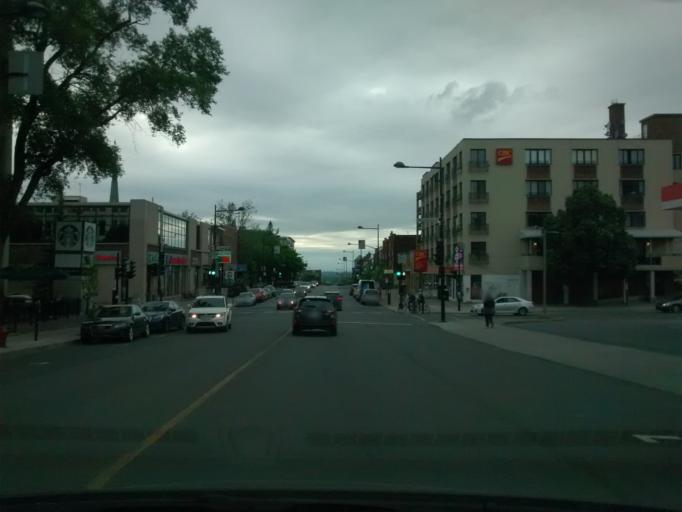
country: CA
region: Quebec
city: Westmount
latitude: 45.4970
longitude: -73.6236
